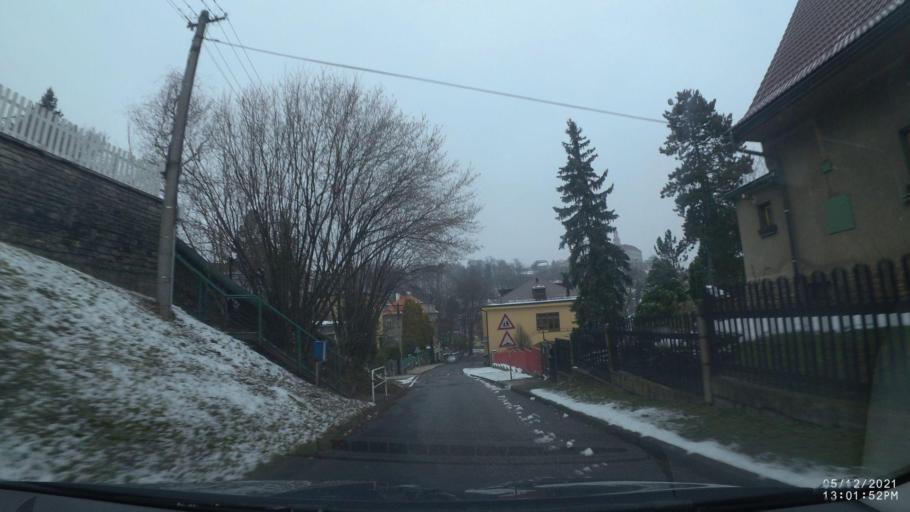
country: CZ
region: Kralovehradecky
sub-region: Okres Nachod
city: Nachod
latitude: 50.4144
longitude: 16.1580
